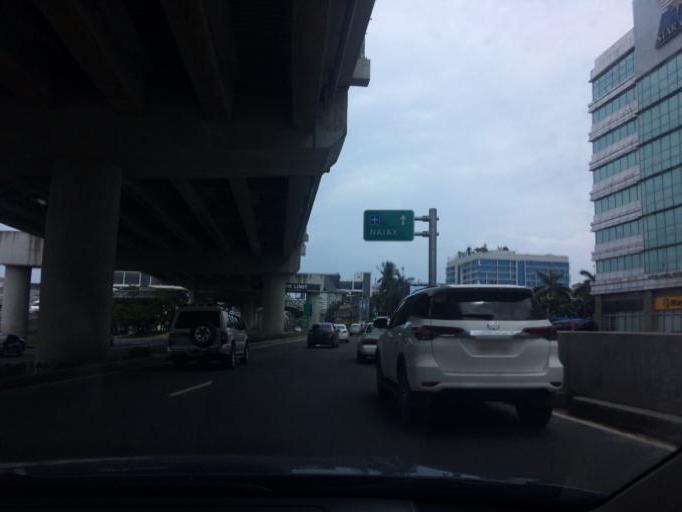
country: PH
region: Metro Manila
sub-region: Makati City
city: Makati City
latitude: 14.5184
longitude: 121.0176
